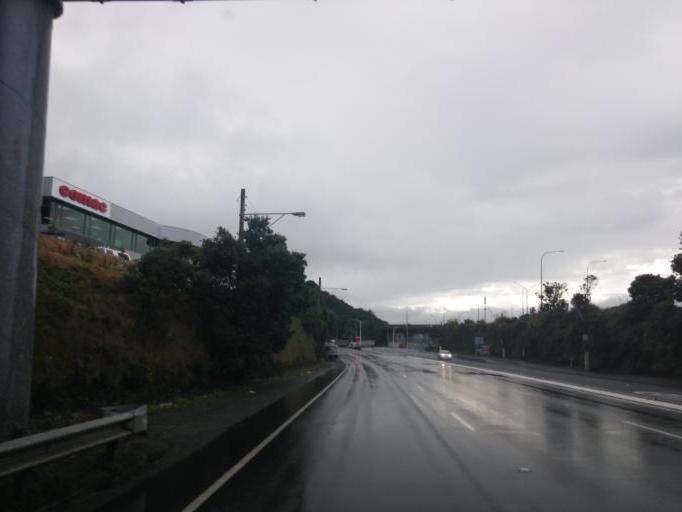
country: NZ
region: Wellington
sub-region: Wellington City
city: Wellington
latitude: -41.2488
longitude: 174.8111
